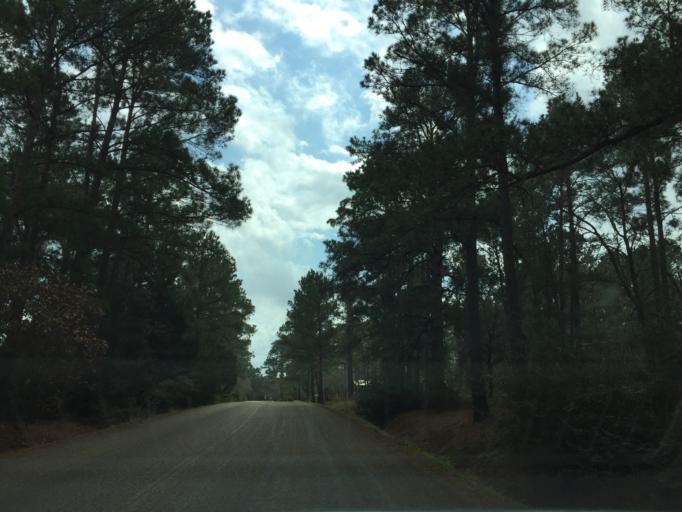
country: US
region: Texas
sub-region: Bastrop County
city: Bastrop
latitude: 30.1248
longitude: -97.2797
